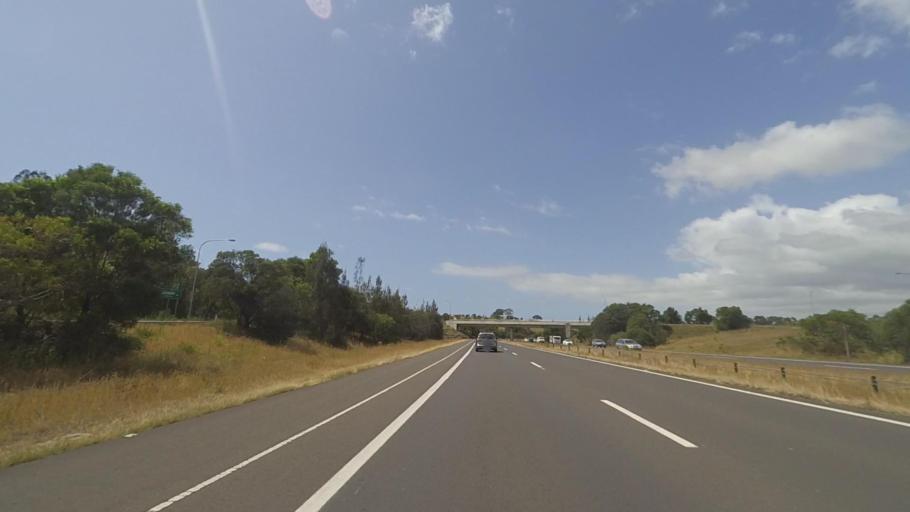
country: AU
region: New South Wales
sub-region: Shellharbour
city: Croom
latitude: -34.6150
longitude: 150.8375
